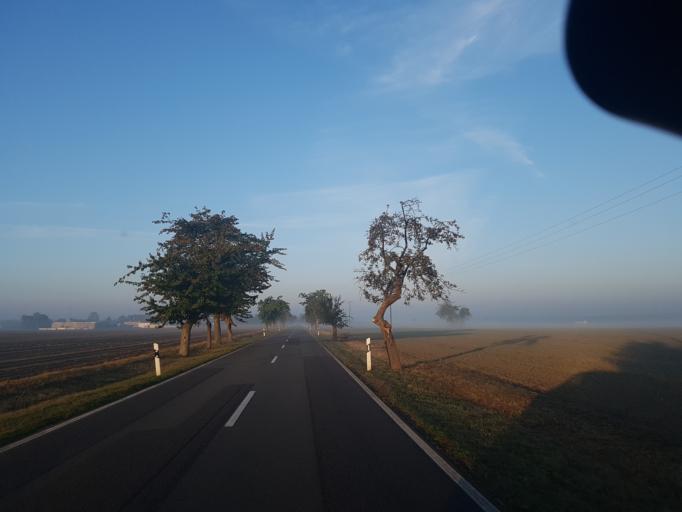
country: DE
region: Brandenburg
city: Juterbog
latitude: 51.8976
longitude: 13.0816
